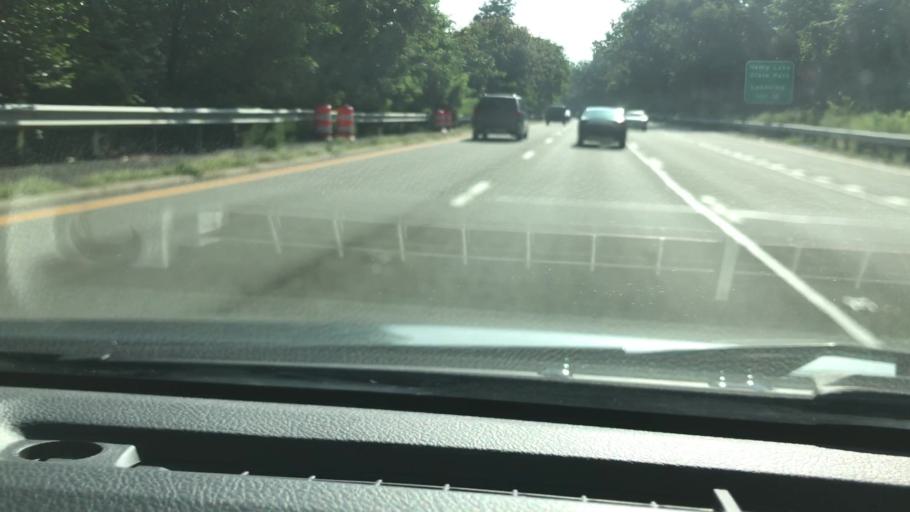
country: US
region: New York
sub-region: Nassau County
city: Lakeview
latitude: 40.6831
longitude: -73.6526
